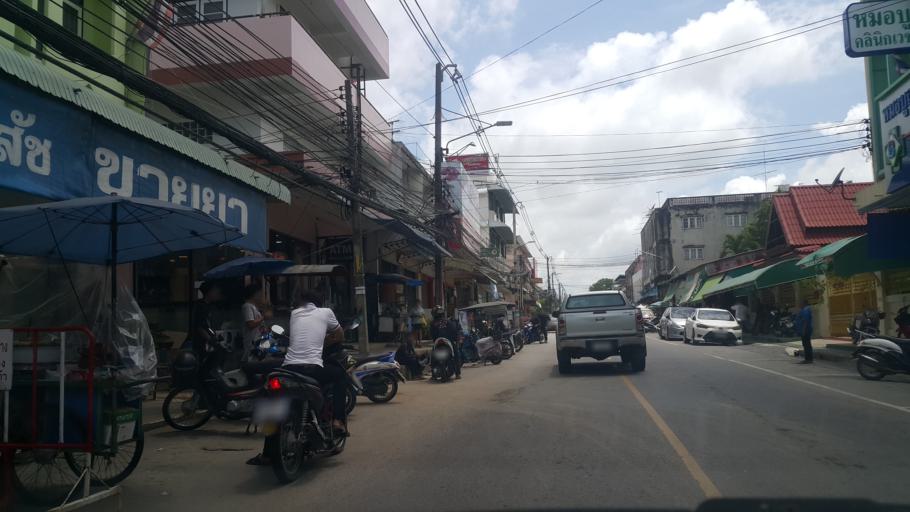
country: TH
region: Rayong
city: Ban Chang
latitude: 12.7256
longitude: 101.0540
